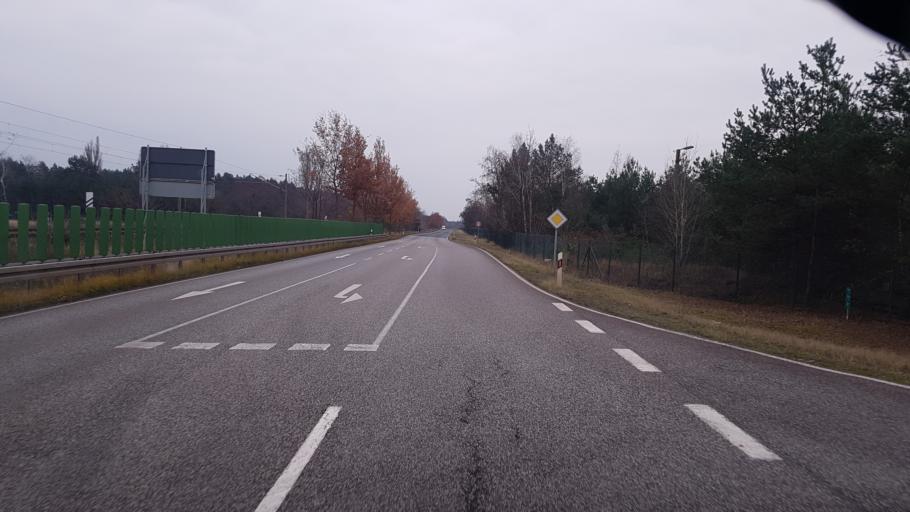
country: DE
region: Brandenburg
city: Eisenhuettenstadt
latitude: 52.1665
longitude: 14.6491
